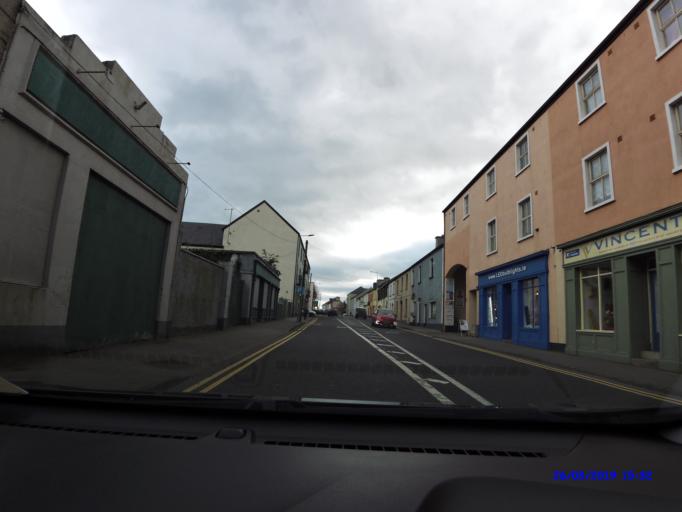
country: IE
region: Connaught
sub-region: Maigh Eo
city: Ballina
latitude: 54.1146
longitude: -9.1584
